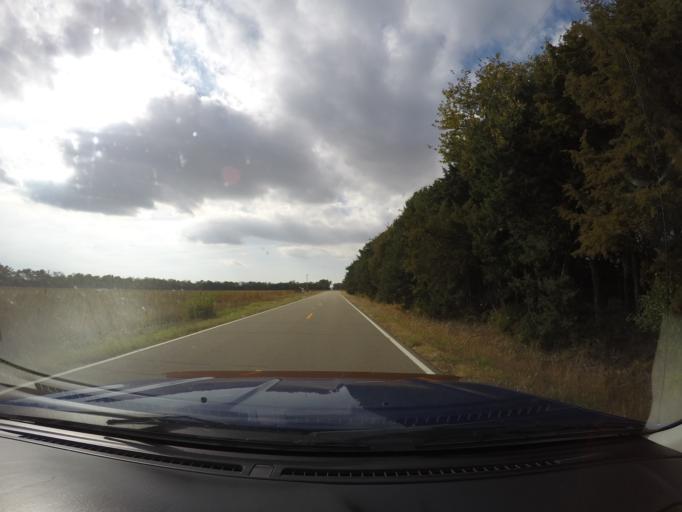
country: US
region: Kansas
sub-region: Saline County
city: Salina
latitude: 38.8417
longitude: -97.6992
